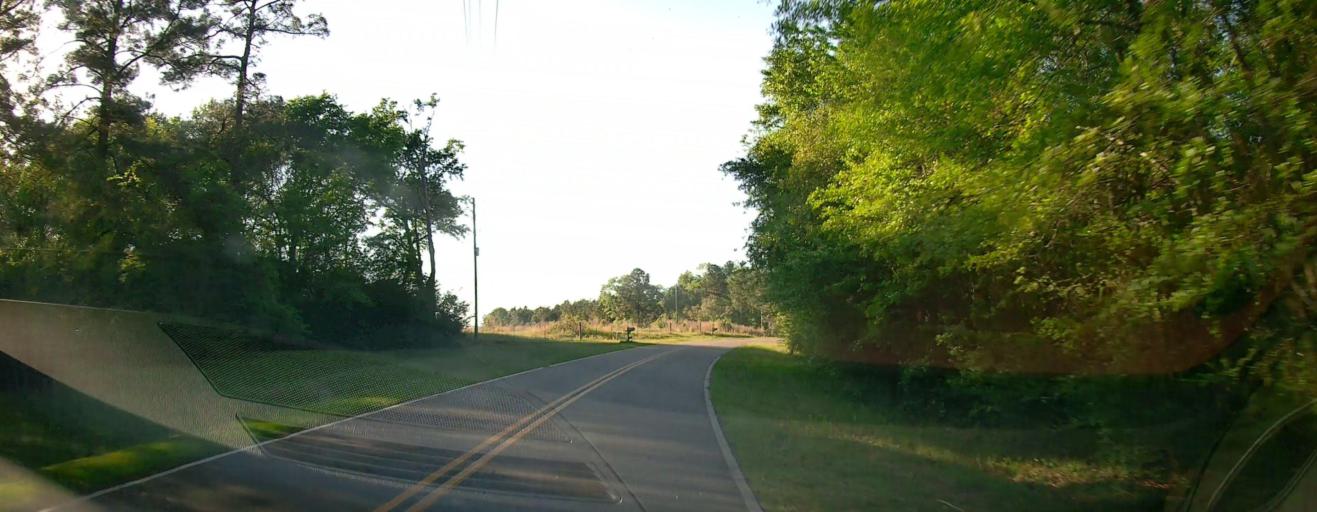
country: US
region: Georgia
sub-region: Macon County
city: Oglethorpe
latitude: 32.2786
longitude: -84.0906
